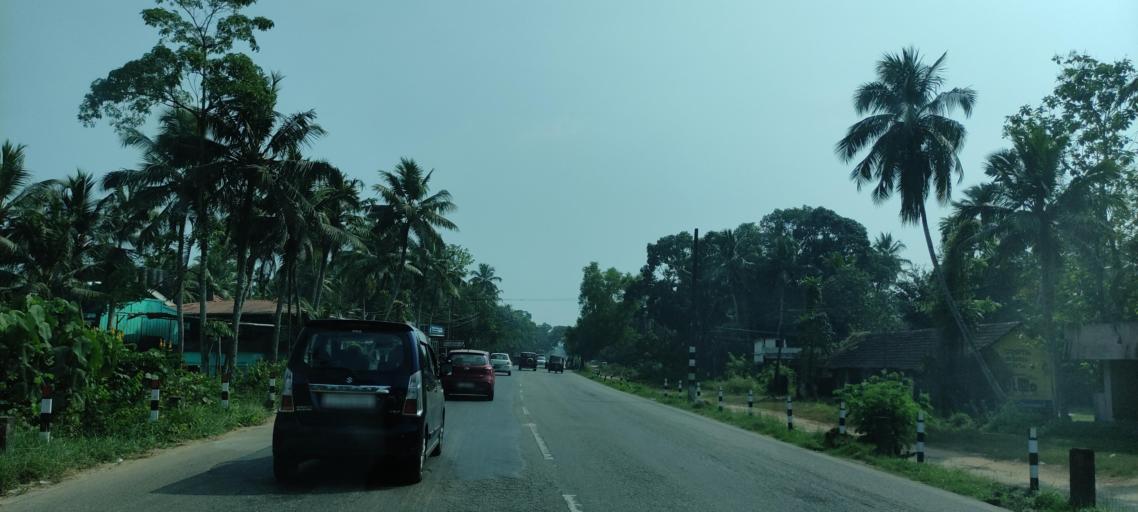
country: IN
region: Kerala
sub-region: Alappuzha
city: Kayankulam
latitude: 9.2251
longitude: 76.4765
